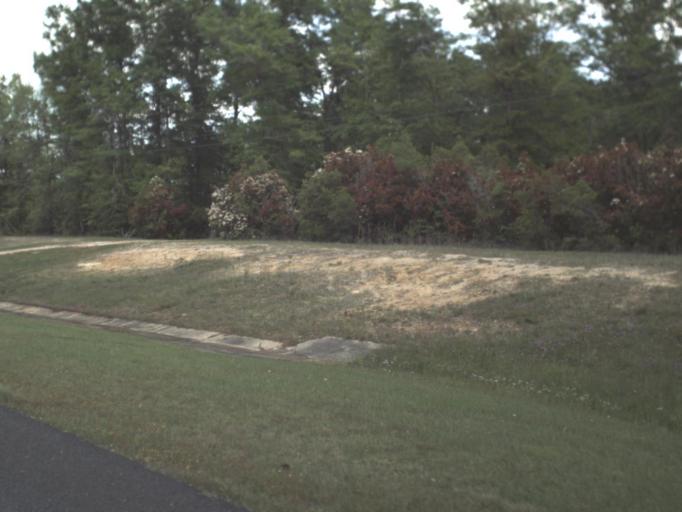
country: US
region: Florida
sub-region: Escambia County
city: Molino
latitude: 30.8196
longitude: -87.3343
